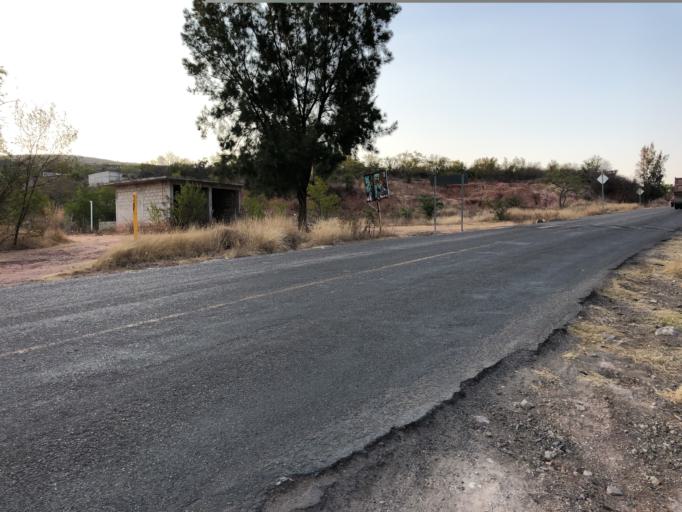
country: MX
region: Oaxaca
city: Ciudad de Huajuapam de Leon
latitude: 17.8382
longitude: -97.7919
